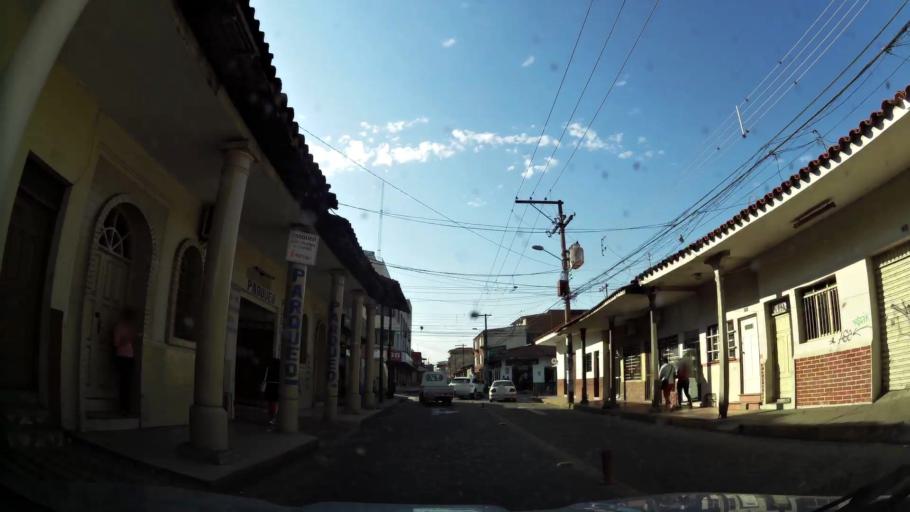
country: BO
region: Santa Cruz
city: Santa Cruz de la Sierra
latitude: -17.7823
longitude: -63.1858
